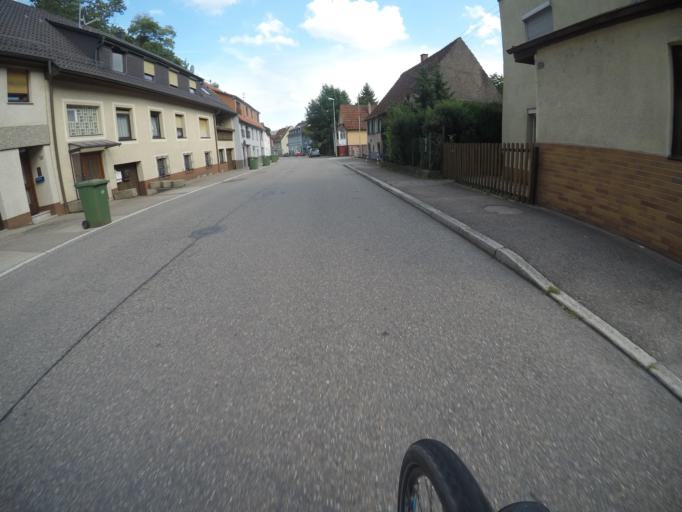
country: DE
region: Baden-Wuerttemberg
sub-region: Karlsruhe Region
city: Niefern-Oschelbronn
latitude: 48.9363
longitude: 8.7938
